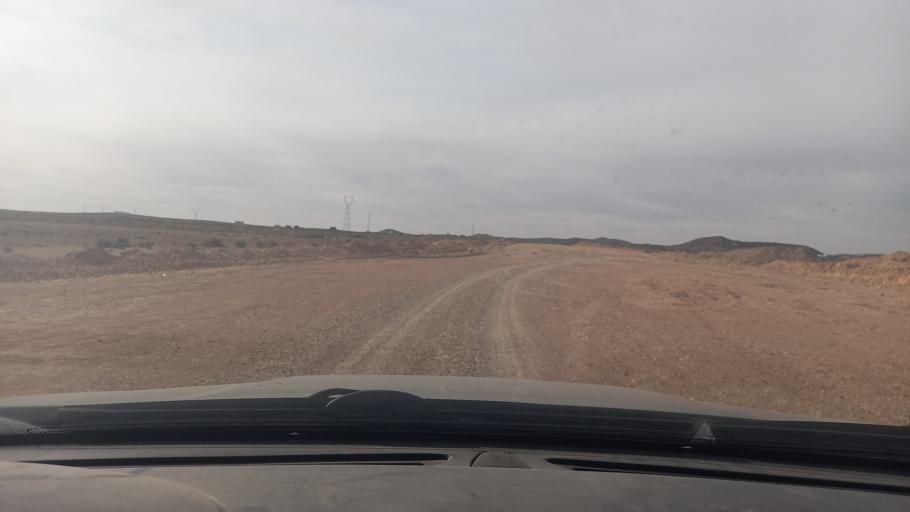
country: TN
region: Tataouine
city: Tataouine
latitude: 33.1306
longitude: 10.5015
